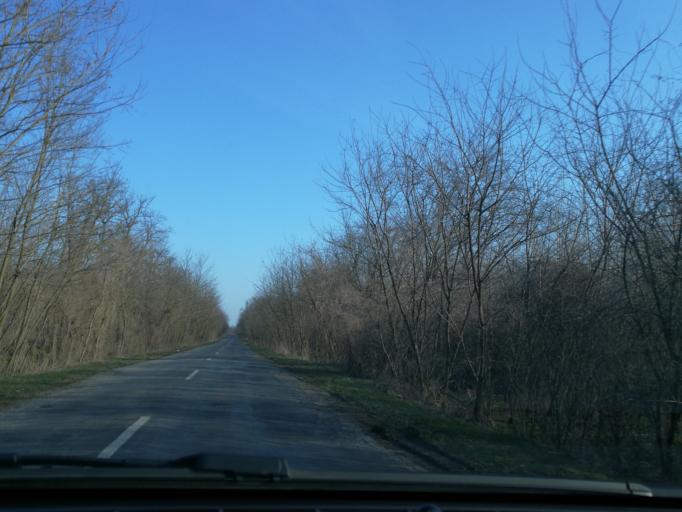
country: HU
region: Szabolcs-Szatmar-Bereg
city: Nyirbogdany
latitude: 48.0376
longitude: 21.9325
